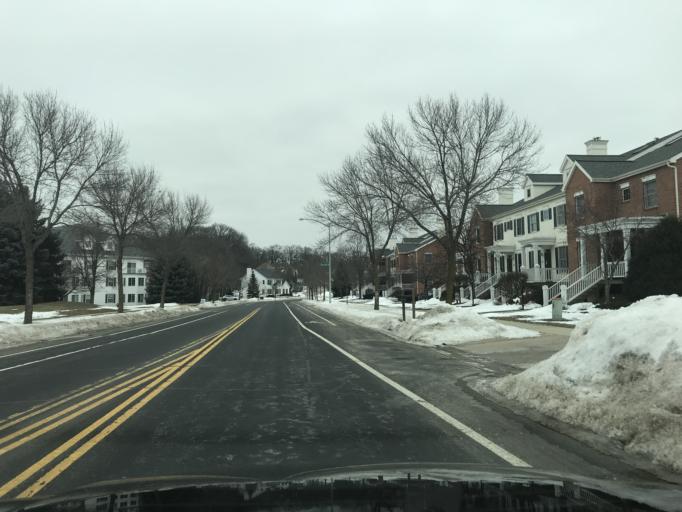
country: US
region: Wisconsin
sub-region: Dane County
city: Monona
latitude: 43.0759
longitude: -89.2764
